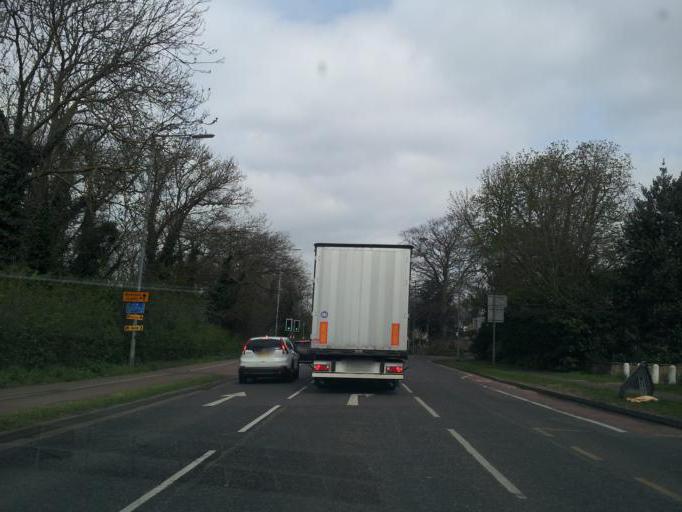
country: GB
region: England
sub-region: Cambridgeshire
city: Cambridge
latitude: 52.1802
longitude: 0.1157
